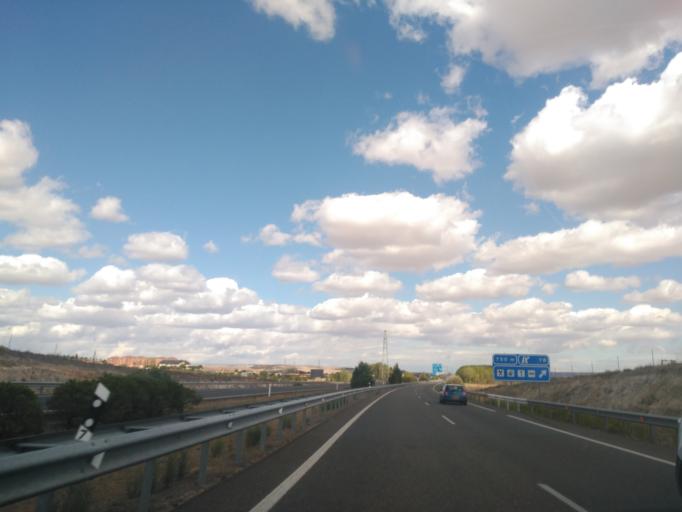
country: ES
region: Castille and Leon
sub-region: Provincia de Palencia
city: Soto de Cerrato
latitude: 41.9752
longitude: -4.4474
